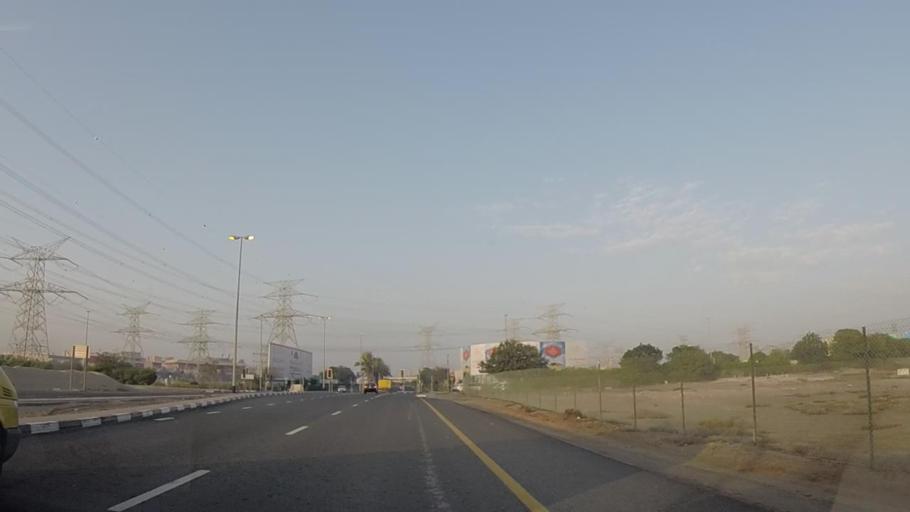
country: AE
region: Dubai
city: Dubai
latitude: 25.0515
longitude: 55.1274
